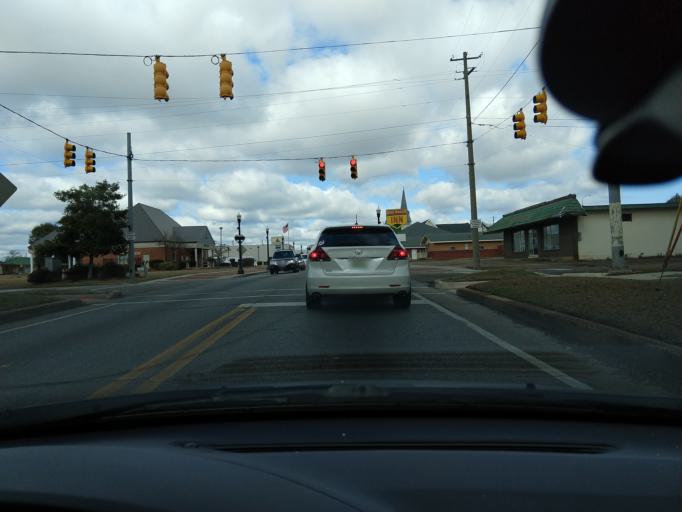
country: US
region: Alabama
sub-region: Coffee County
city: Enterprise
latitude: 31.3114
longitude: -85.8515
